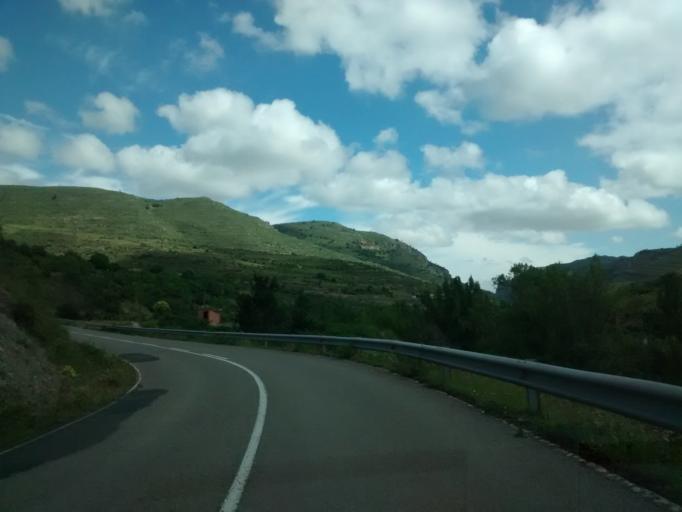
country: ES
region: La Rioja
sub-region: Provincia de La Rioja
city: Soto en Cameros
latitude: 42.2789
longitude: -2.4326
